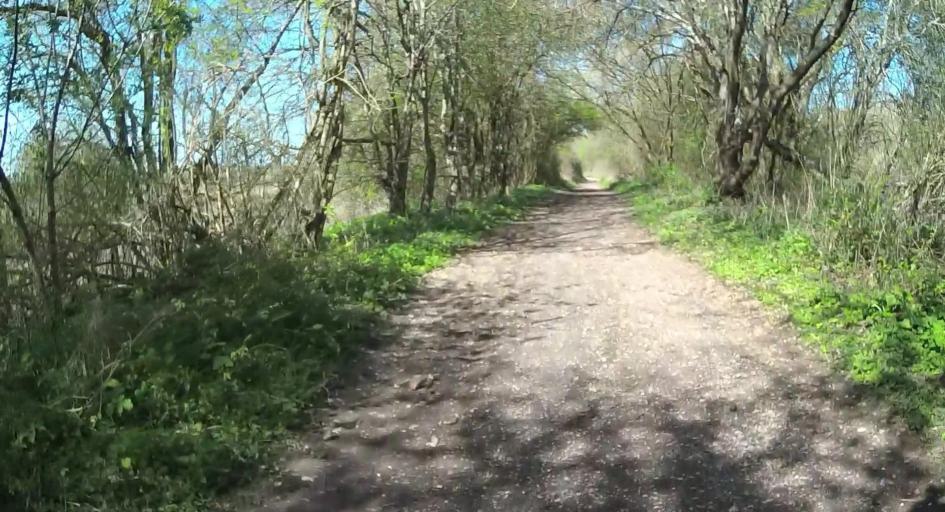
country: GB
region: England
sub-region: Hampshire
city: Abbotts Ann
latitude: 51.1064
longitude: -1.4933
